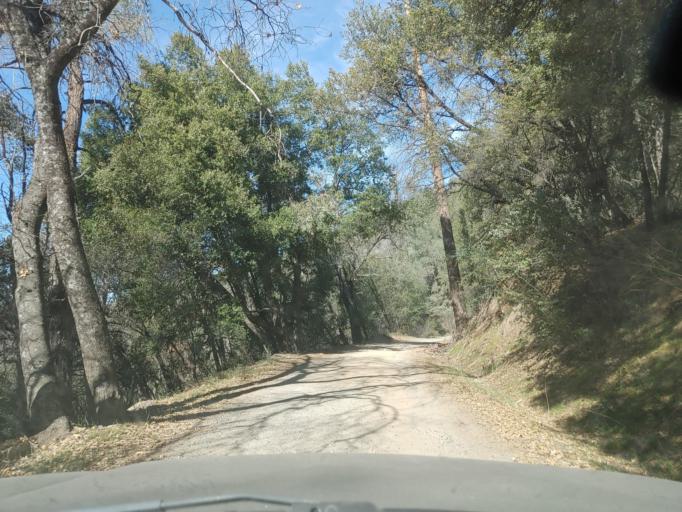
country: US
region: California
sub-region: Madera County
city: Ahwahnee
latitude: 37.4136
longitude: -119.7027
